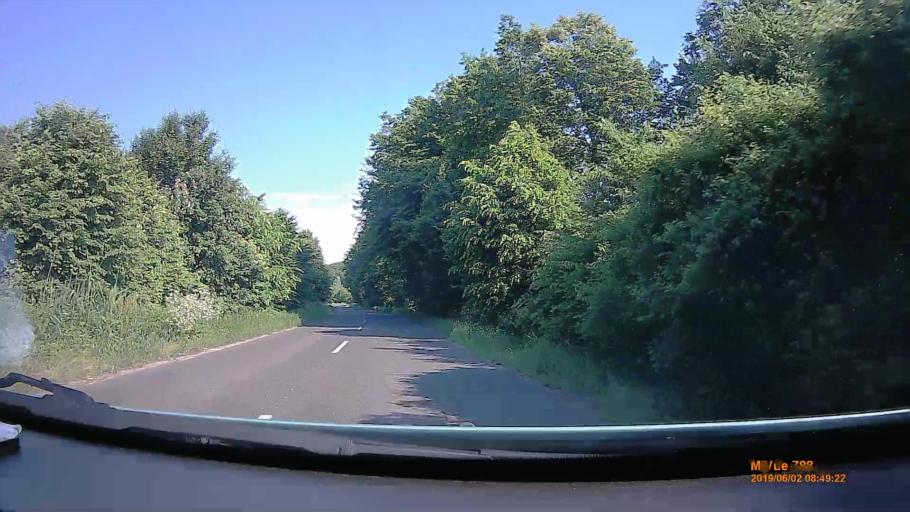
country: HU
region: Borsod-Abauj-Zemplen
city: Sajobabony
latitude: 48.1425
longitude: 20.6984
